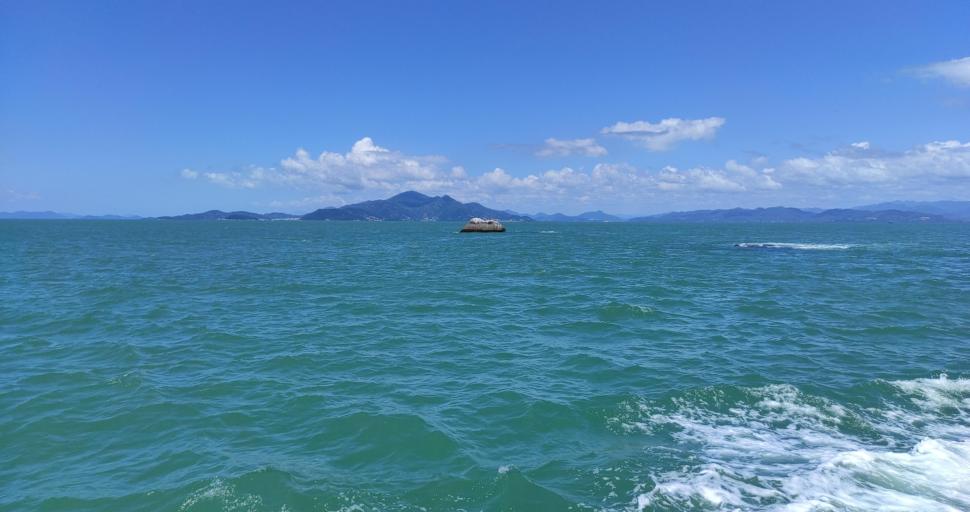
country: BR
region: Santa Catarina
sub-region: Porto Belo
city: Porto Belo
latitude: -27.2222
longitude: -48.5119
